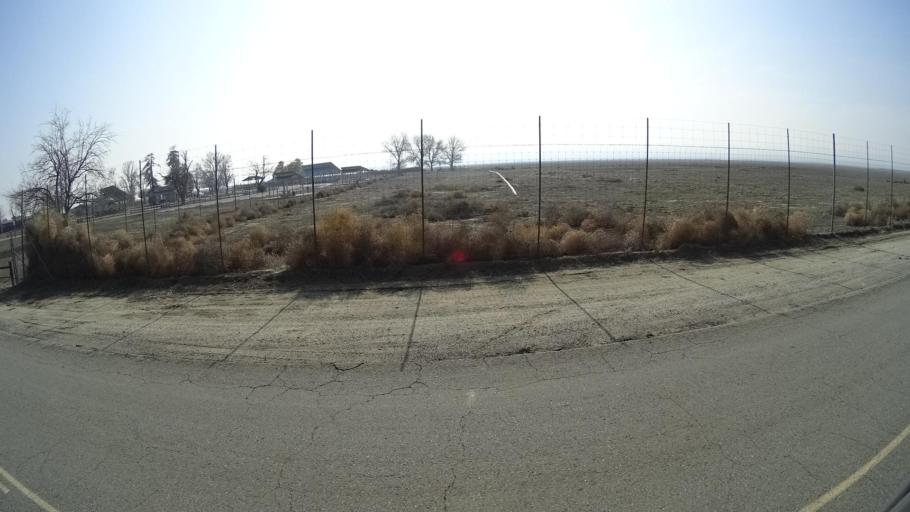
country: US
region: California
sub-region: Kern County
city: Buttonwillow
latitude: 35.3334
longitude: -119.3647
